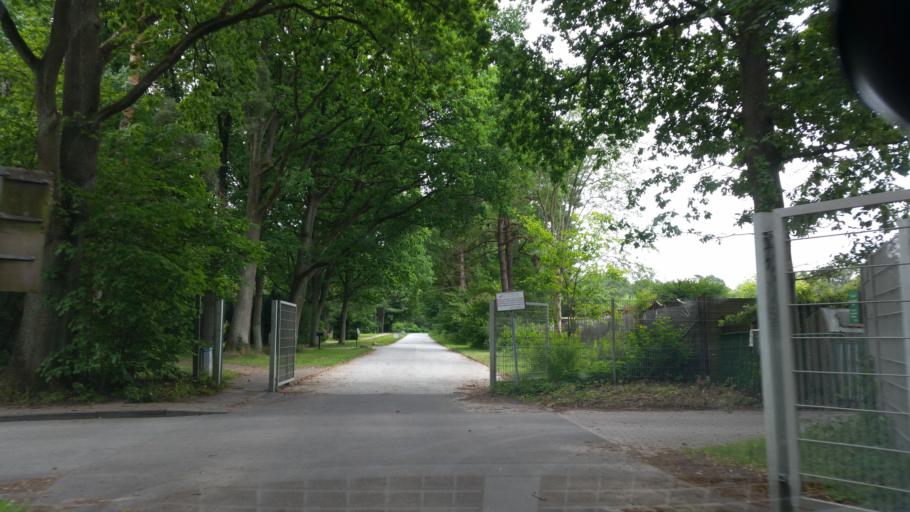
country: DE
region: Schleswig-Holstein
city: Wentorf bei Hamburg
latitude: 53.4815
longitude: 10.2518
